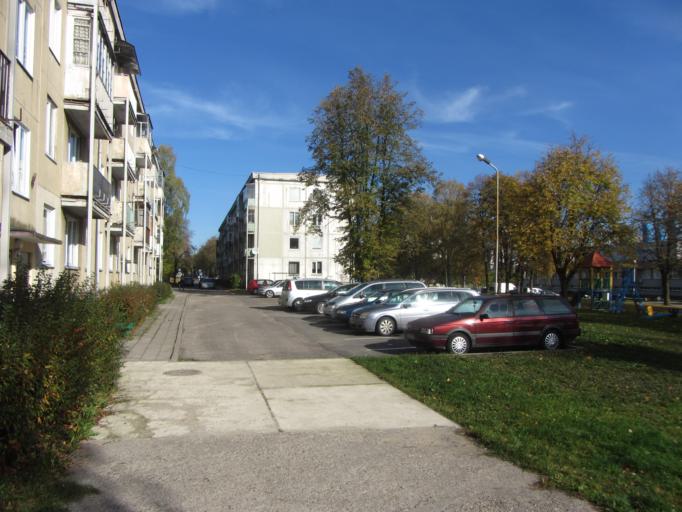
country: LT
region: Vilnius County
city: Elektrenai
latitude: 54.7834
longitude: 24.6646
